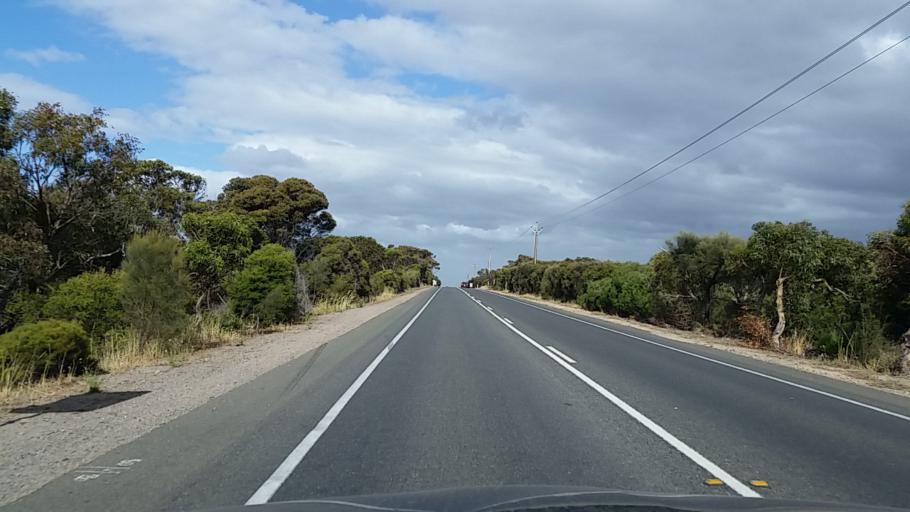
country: AU
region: South Australia
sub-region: Alexandrina
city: Goolwa
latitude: -35.5058
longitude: 138.7638
